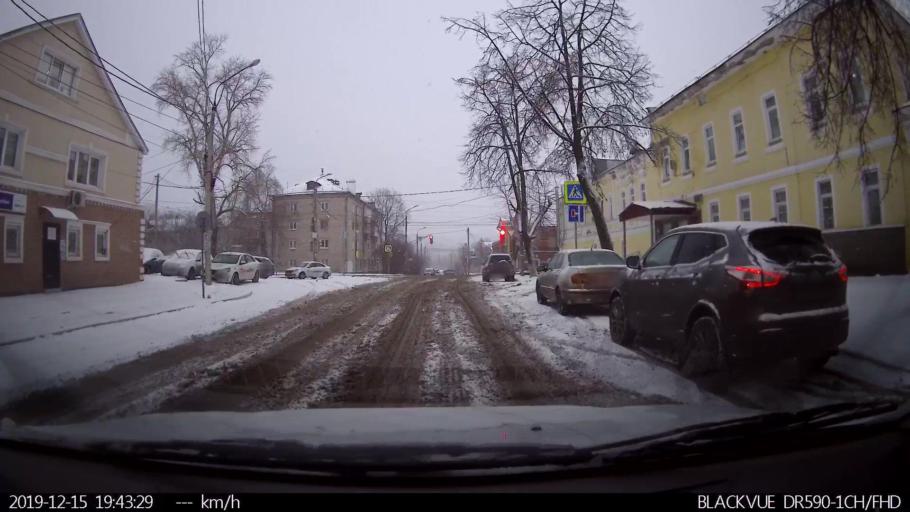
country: RU
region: Nizjnij Novgorod
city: Sarov
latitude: 54.9608
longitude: 43.5446
